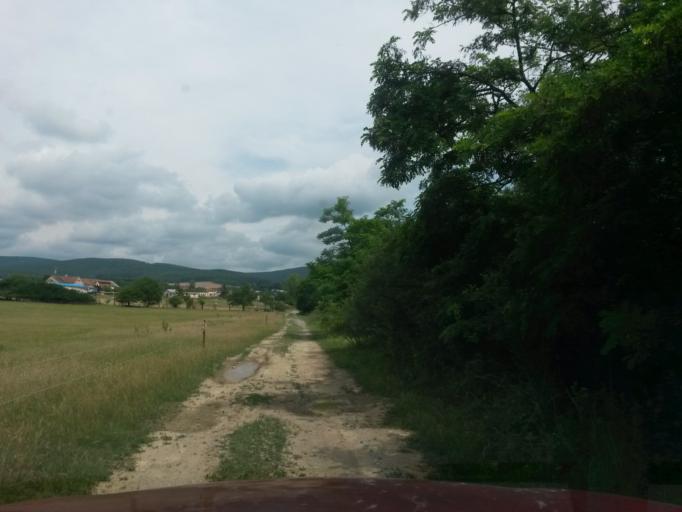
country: SK
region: Kosicky
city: Moldava nad Bodvou
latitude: 48.6668
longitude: 21.1123
